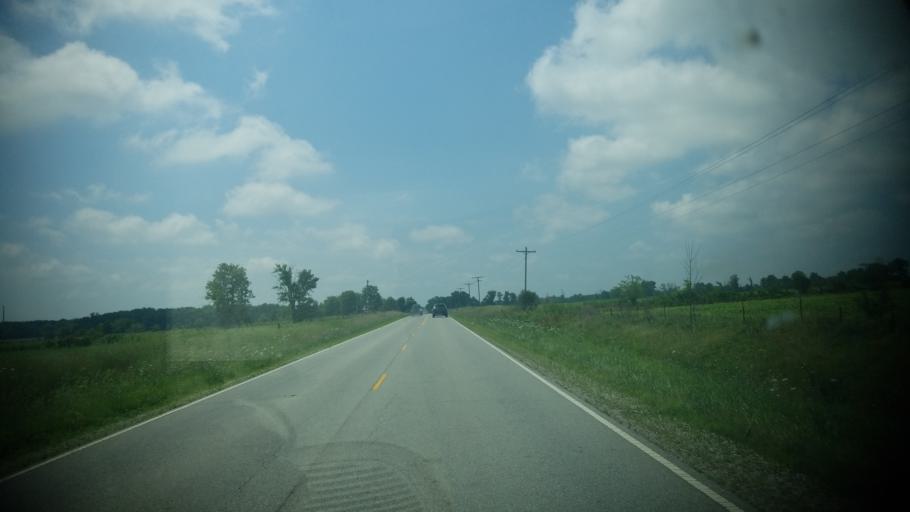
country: US
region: Illinois
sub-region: Wayne County
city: Fairfield
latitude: 38.4726
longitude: -88.3489
